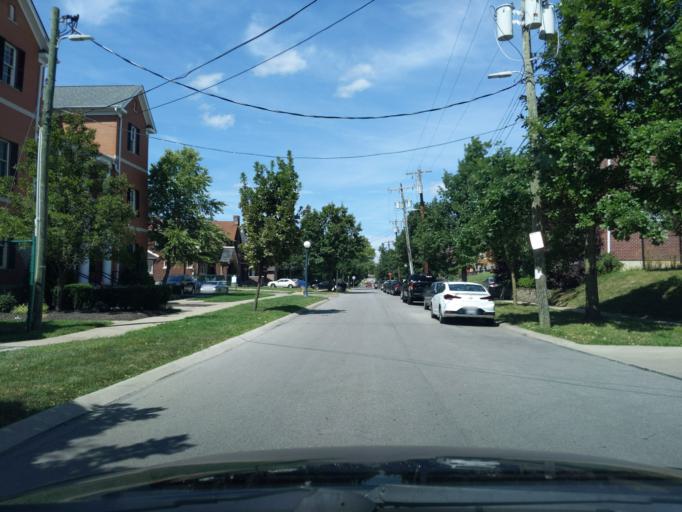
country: US
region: Ohio
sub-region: Hamilton County
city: Saint Bernard
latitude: 39.1319
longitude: -84.5220
